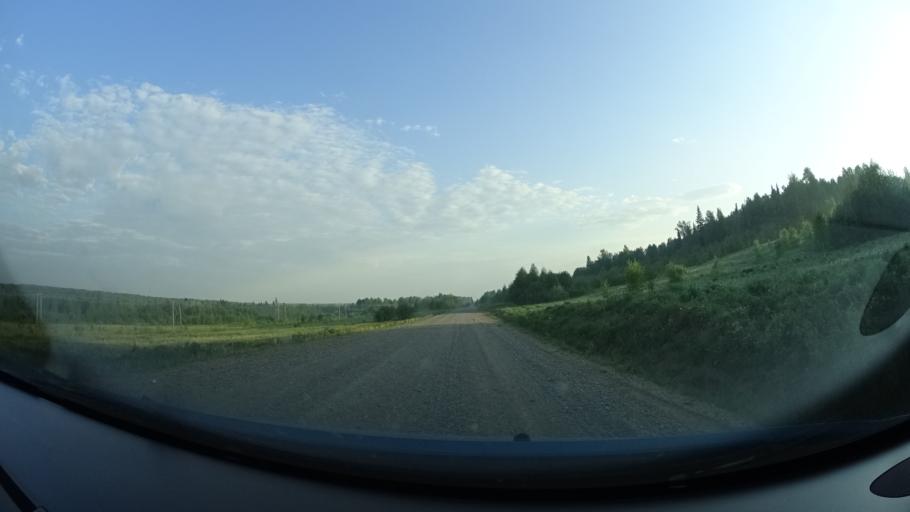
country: RU
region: Perm
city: Barda
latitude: 56.7028
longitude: 55.6801
